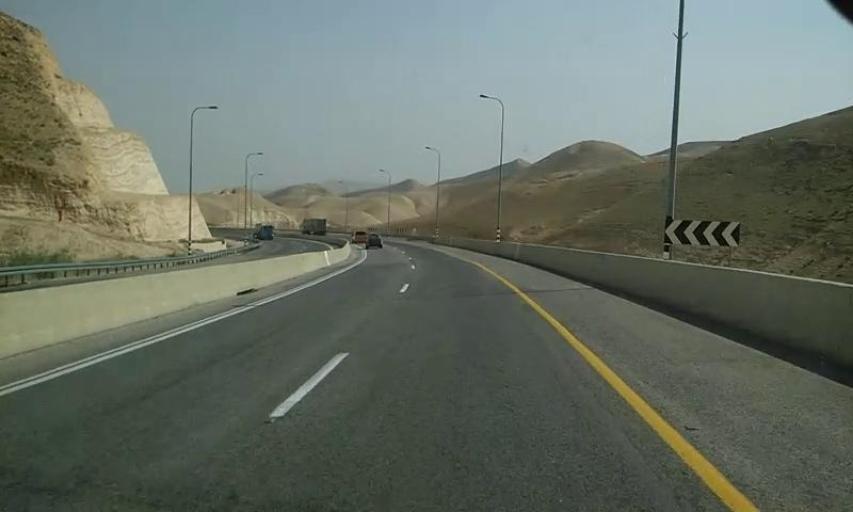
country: PS
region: West Bank
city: Jericho
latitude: 31.8092
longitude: 35.3920
